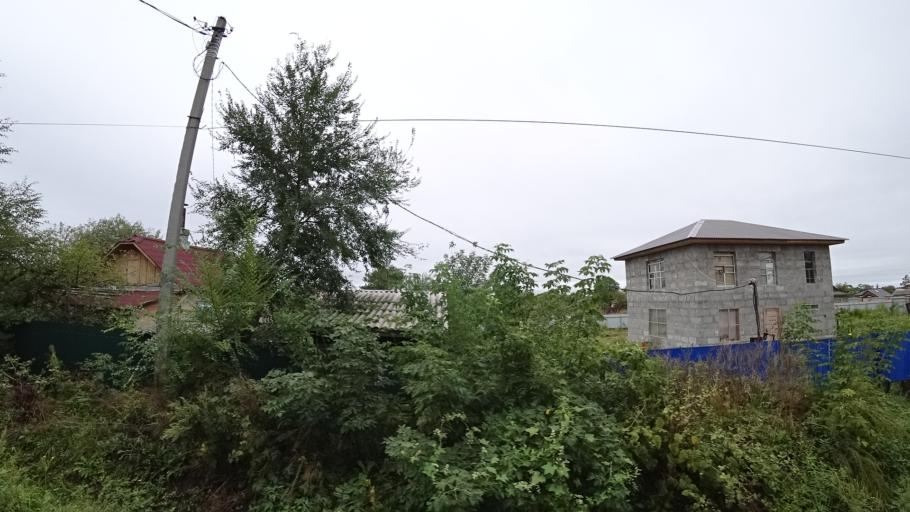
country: RU
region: Primorskiy
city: Monastyrishche
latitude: 44.1962
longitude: 132.4971
